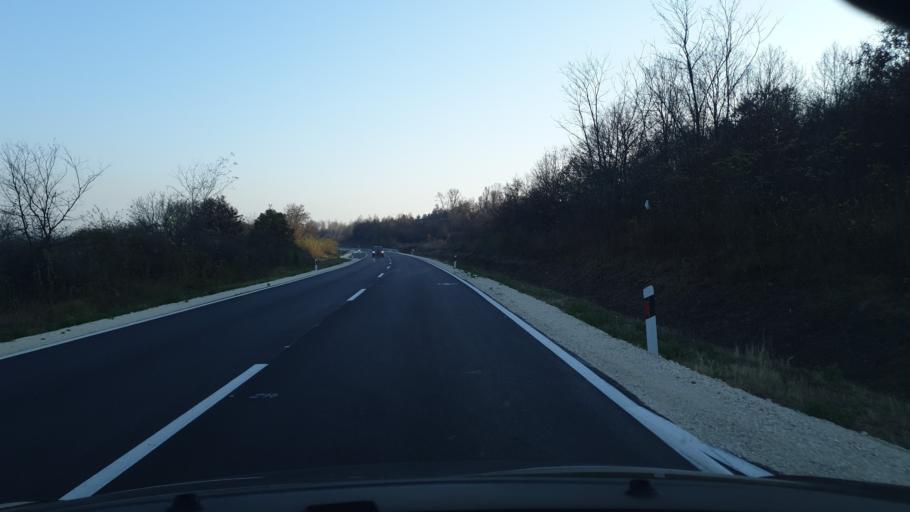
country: RS
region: Central Serbia
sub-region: Zajecarski Okrug
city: Zajecar
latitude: 43.9683
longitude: 22.2940
